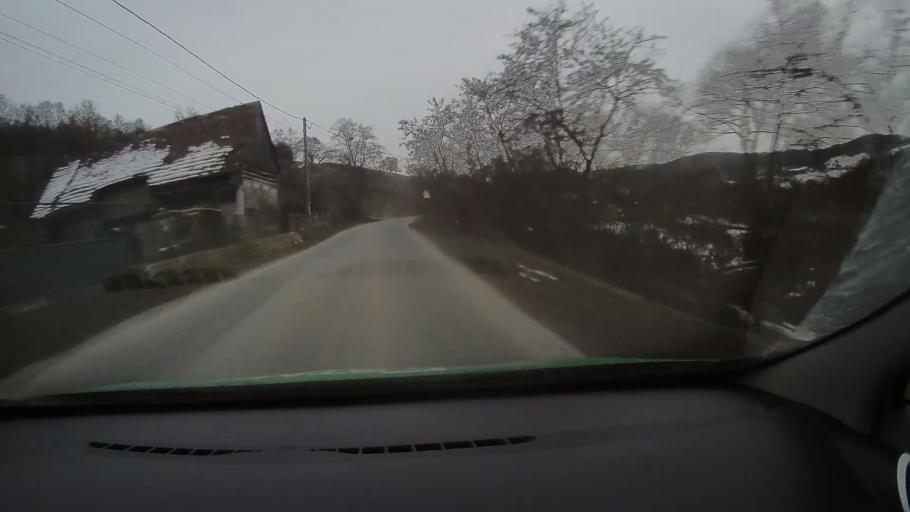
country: RO
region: Harghita
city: Taureni
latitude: 46.2566
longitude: 25.2525
